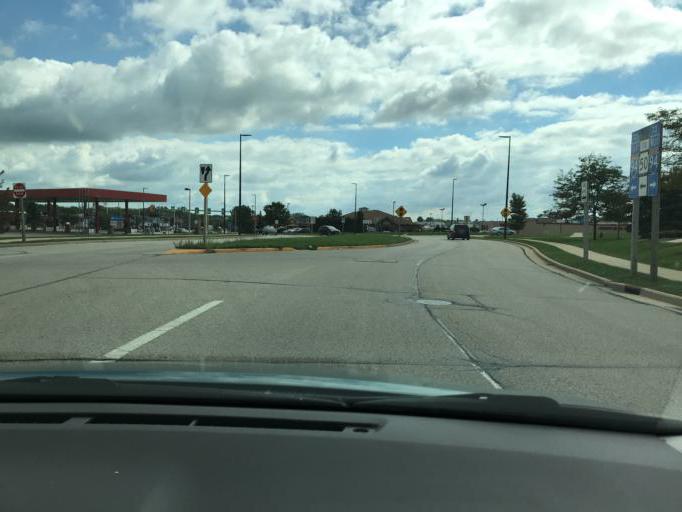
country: US
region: Wisconsin
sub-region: Kenosha County
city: Pleasant Prairie
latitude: 42.5700
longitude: -87.9501
